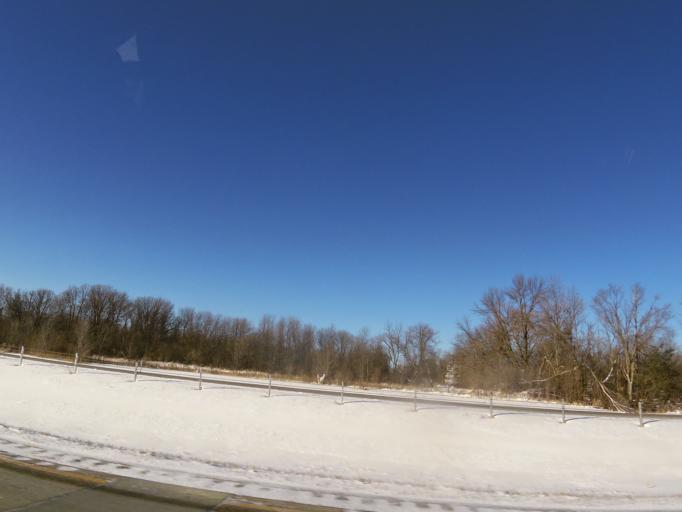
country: US
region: Minnesota
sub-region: Rice County
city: Faribault
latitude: 44.3412
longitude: -93.2931
